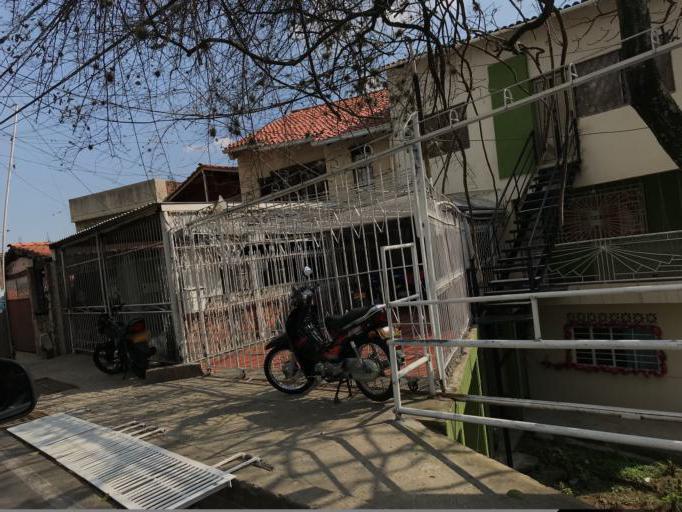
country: CO
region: Valle del Cauca
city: Cali
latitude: 3.4506
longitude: -76.5635
